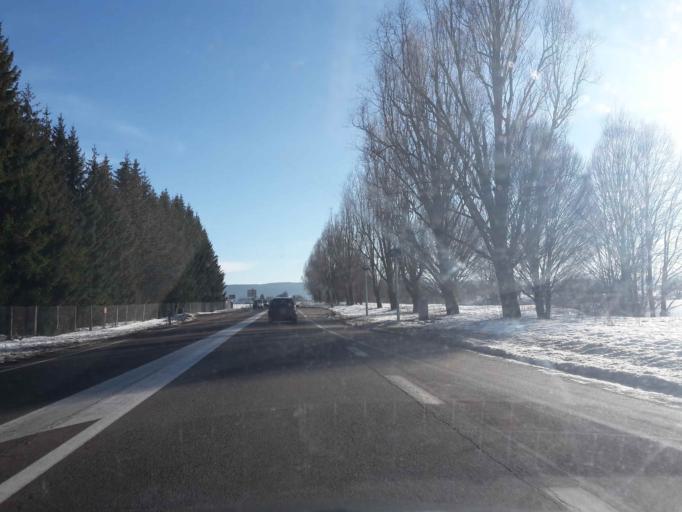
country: FR
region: Franche-Comte
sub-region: Departement du Doubs
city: Doubs
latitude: 46.9415
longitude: 6.3431
